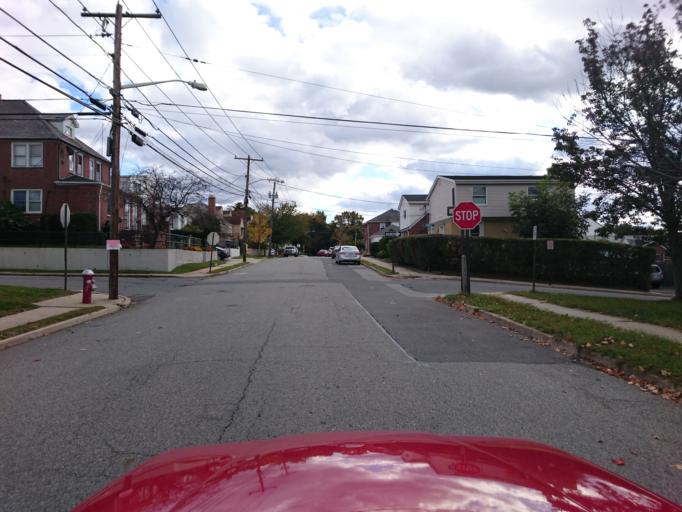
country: US
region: New York
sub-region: Nassau County
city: Glen Cove
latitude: 40.8553
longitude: -73.6157
